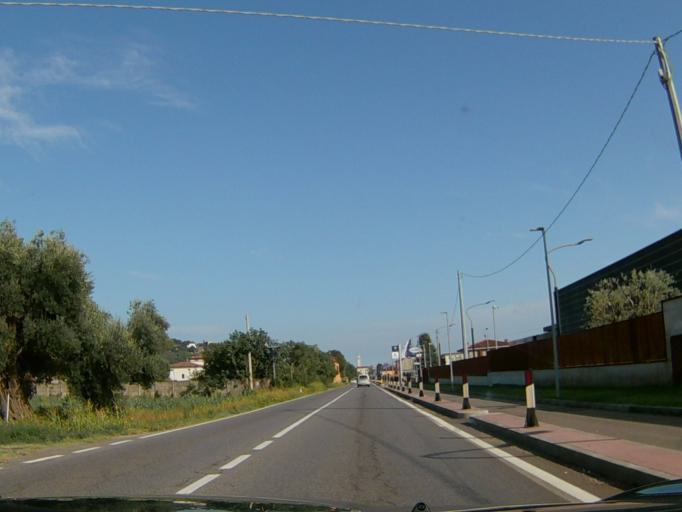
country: IT
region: Lombardy
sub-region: Provincia di Brescia
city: Coccaglio
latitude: 45.5699
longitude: 9.9608
